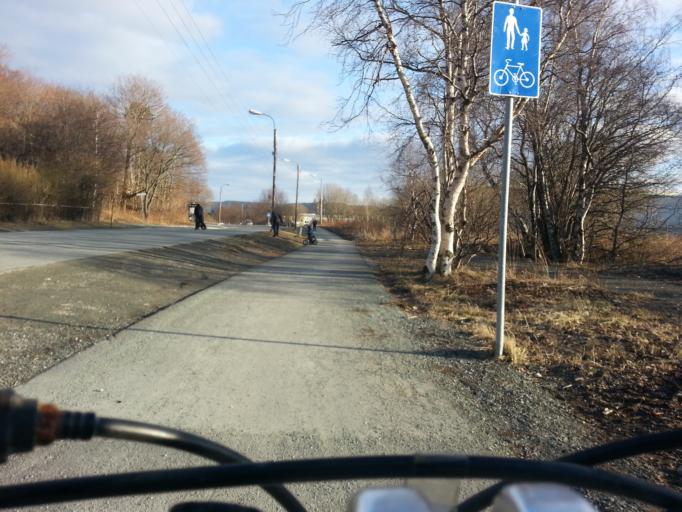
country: NO
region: Sor-Trondelag
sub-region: Trondheim
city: Trondheim
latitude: 63.4453
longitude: 10.4555
